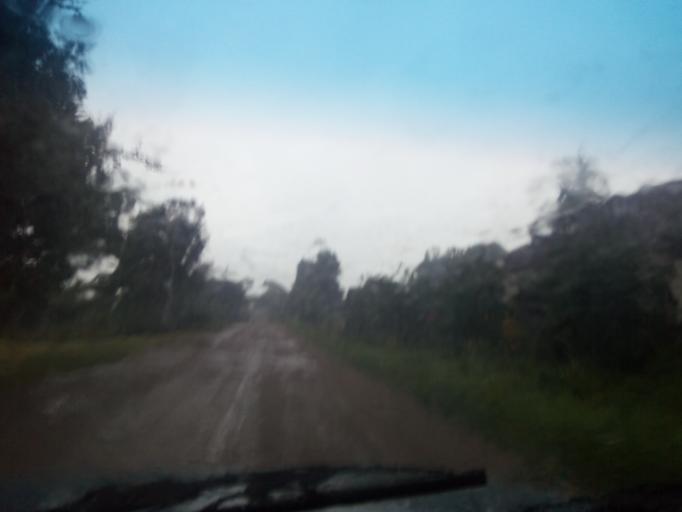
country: BY
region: Vitebsk
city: Dzisna
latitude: 55.6715
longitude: 28.3211
